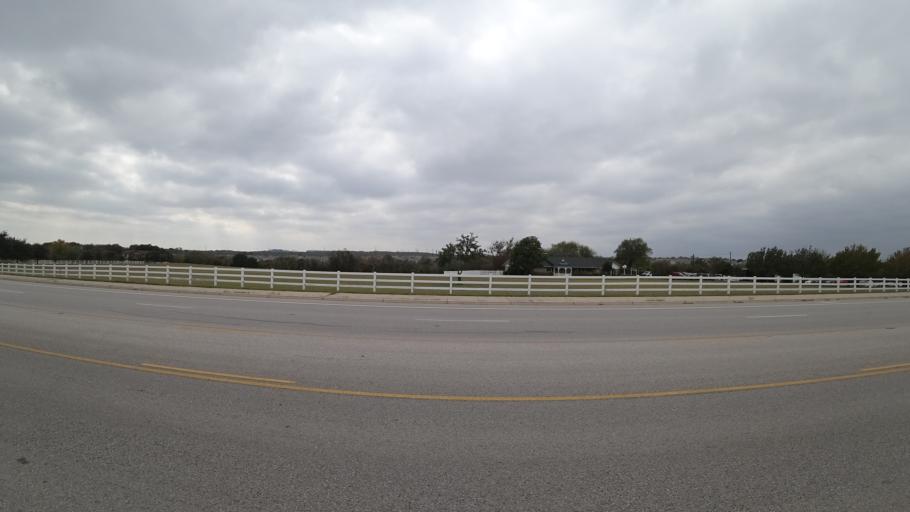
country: US
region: Texas
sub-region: Travis County
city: Pflugerville
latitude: 30.3941
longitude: -97.6285
